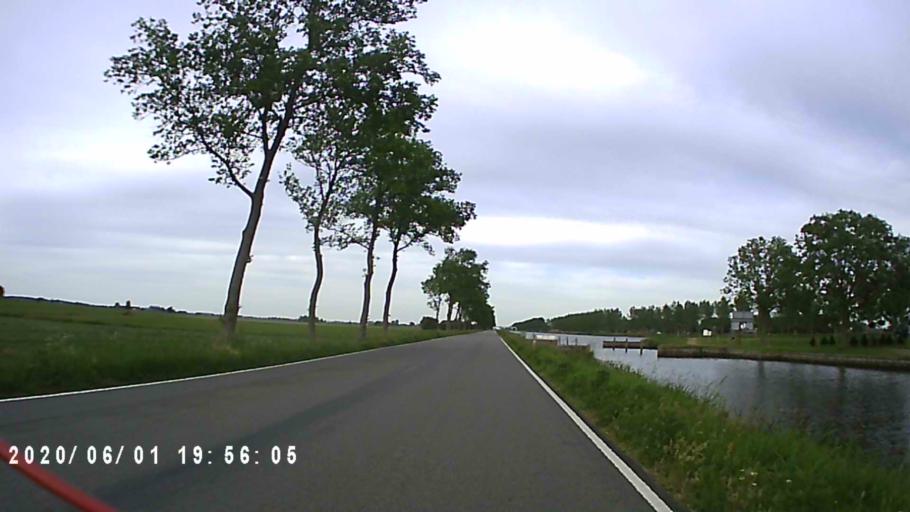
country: NL
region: Friesland
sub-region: Gemeente Achtkarspelen
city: Surhuizum
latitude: 53.2393
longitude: 6.2216
